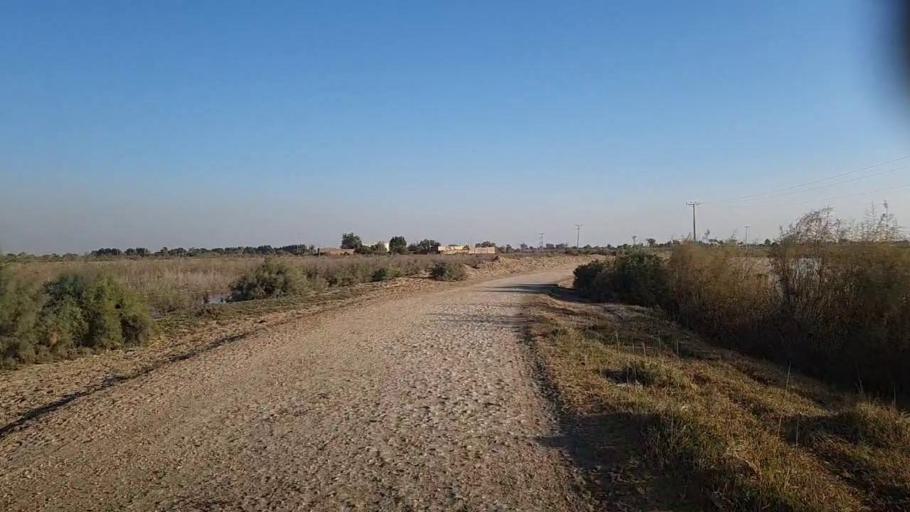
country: PK
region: Sindh
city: Khairpur
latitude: 27.8901
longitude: 69.7070
